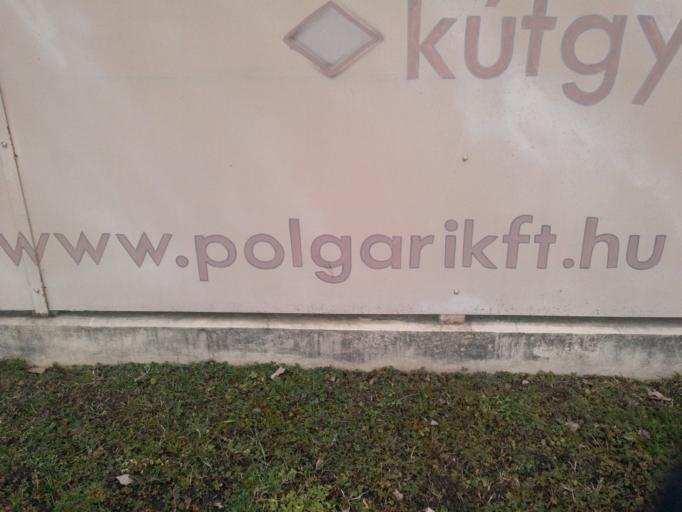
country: HU
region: Borsod-Abauj-Zemplen
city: Encs
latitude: 48.3298
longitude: 21.1331
